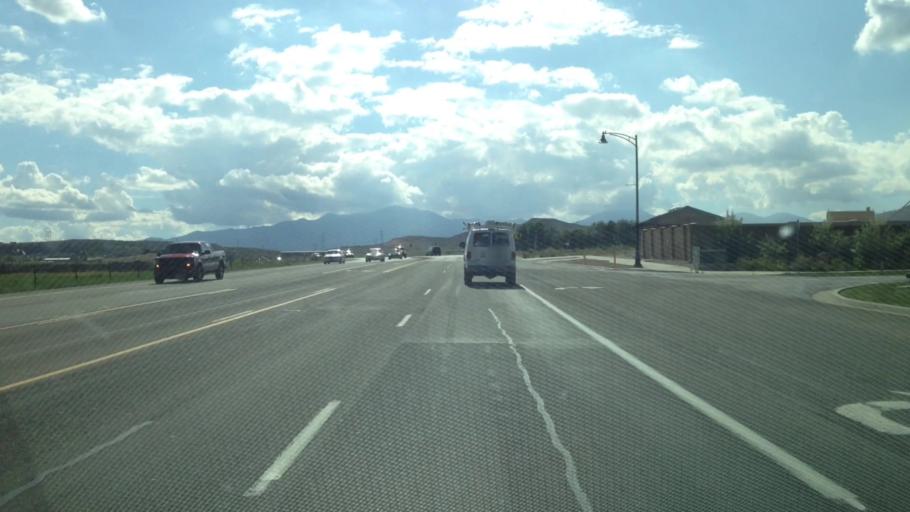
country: US
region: Utah
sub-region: Utah County
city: Saratoga Springs
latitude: 40.3876
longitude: -111.9252
